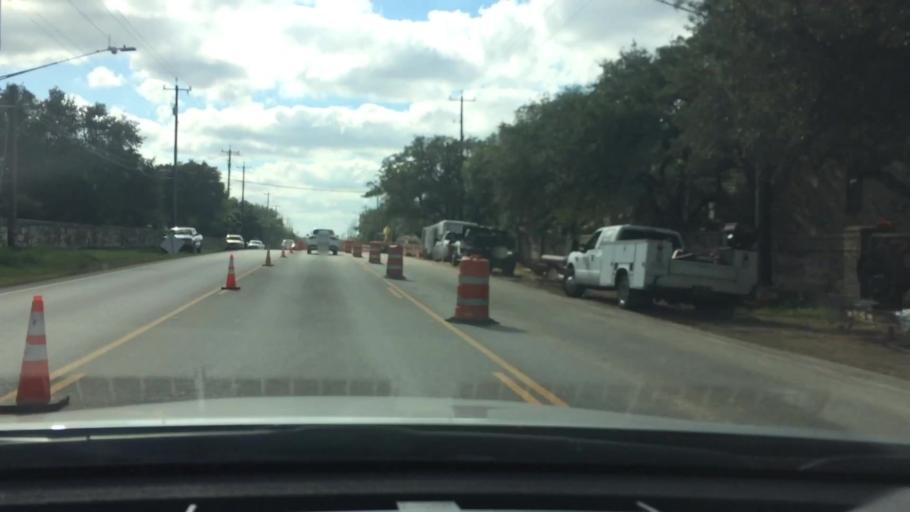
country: US
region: Texas
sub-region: Bexar County
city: Shavano Park
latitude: 29.5737
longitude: -98.5696
